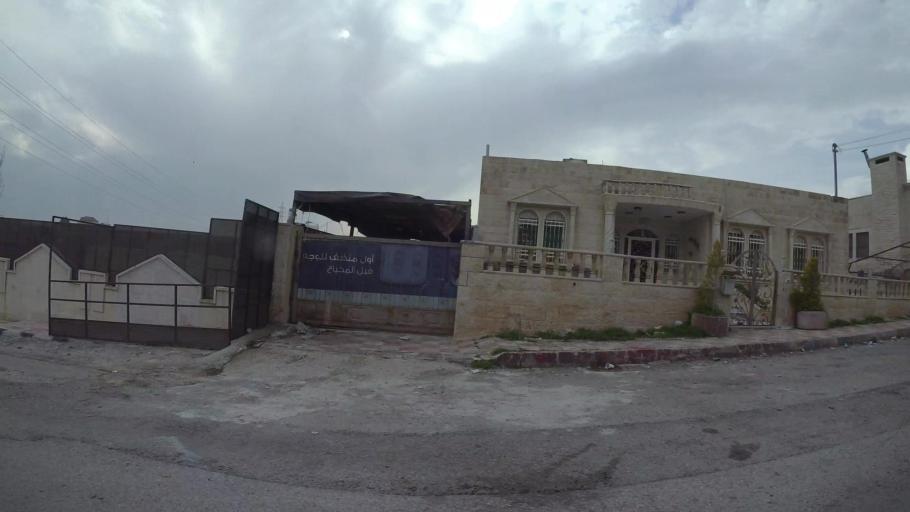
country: JO
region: Amman
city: Umm as Summaq
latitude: 31.8833
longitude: 35.8699
